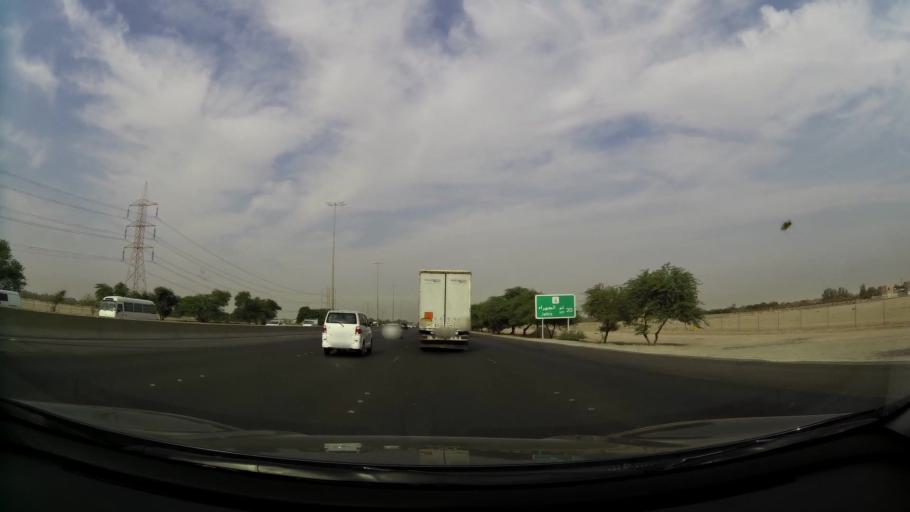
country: KW
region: Al Asimah
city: Ar Rabiyah
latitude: 29.2706
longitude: 47.8206
